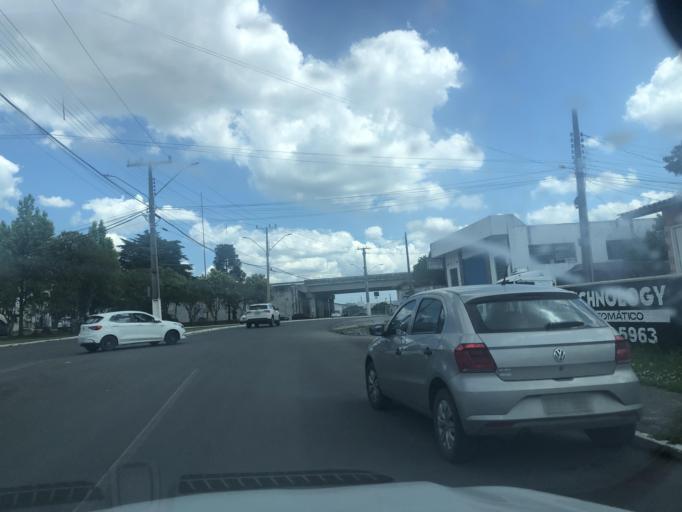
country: BR
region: Santa Catarina
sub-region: Lages
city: Lages
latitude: -27.7965
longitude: -50.3110
